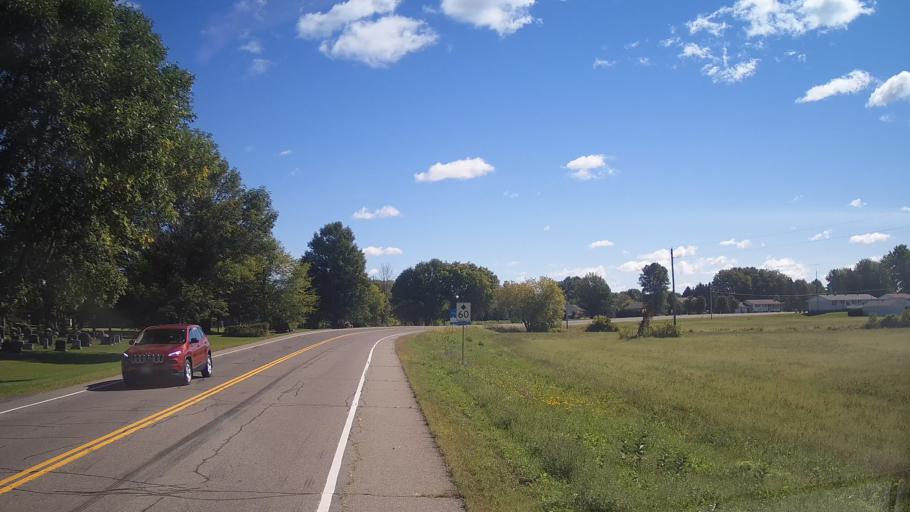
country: US
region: New York
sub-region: St. Lawrence County
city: Norfolk
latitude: 44.9729
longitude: -75.2567
